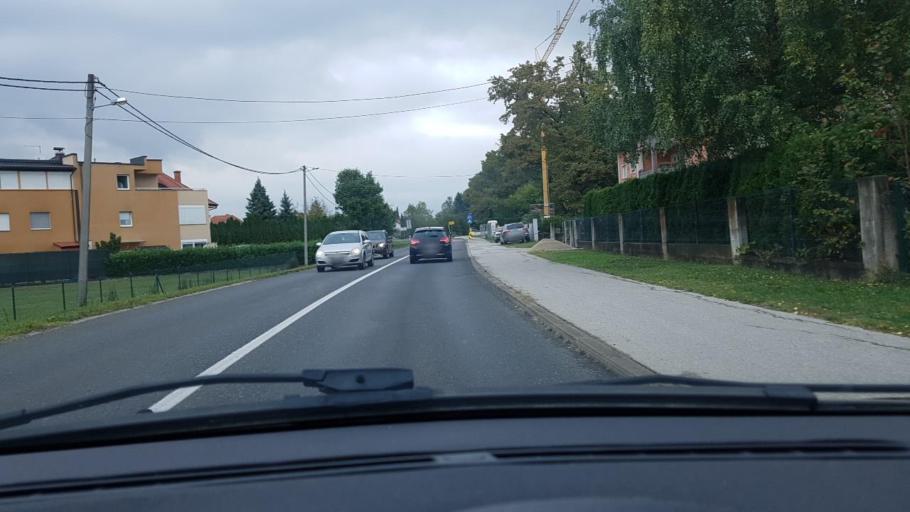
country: HR
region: Grad Zagreb
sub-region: Sesvete
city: Sesvete
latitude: 45.8448
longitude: 16.1091
